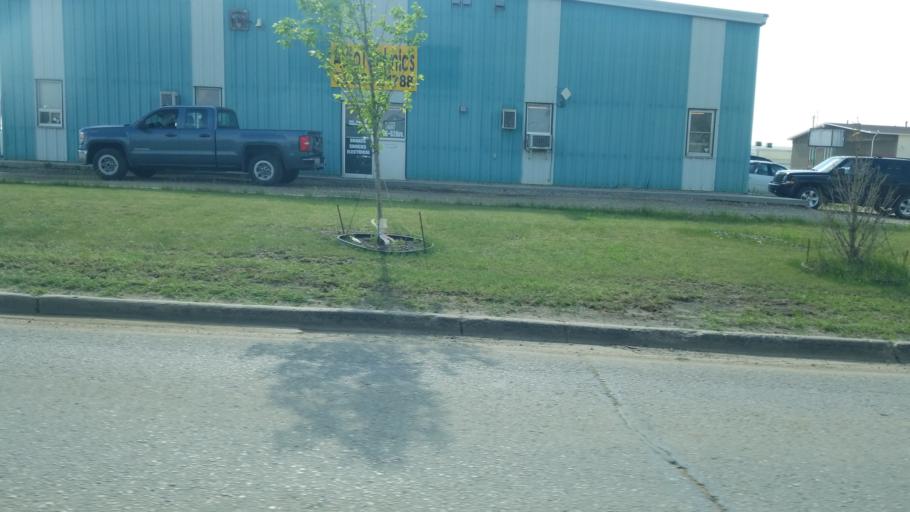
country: CA
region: Saskatchewan
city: Lloydminster
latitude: 53.2819
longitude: -110.0340
